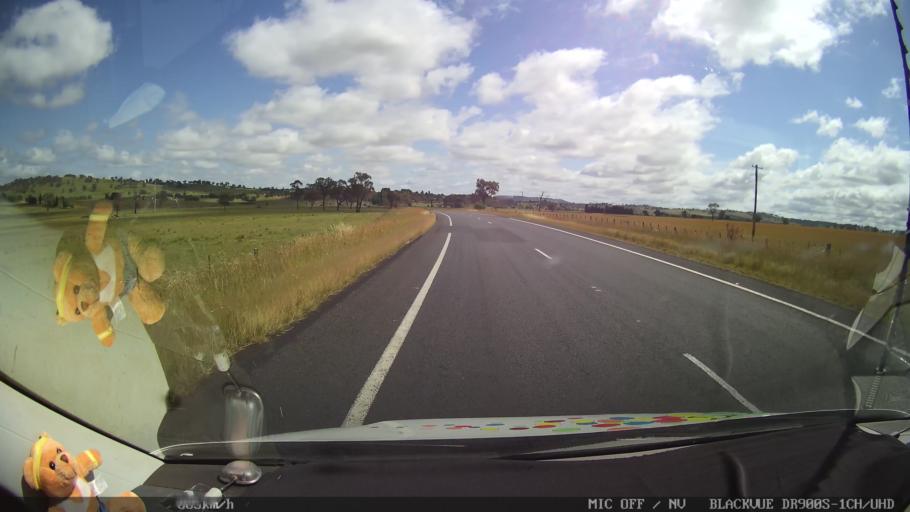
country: AU
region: New South Wales
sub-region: Glen Innes Severn
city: Glen Innes
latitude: -29.9420
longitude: 151.7226
